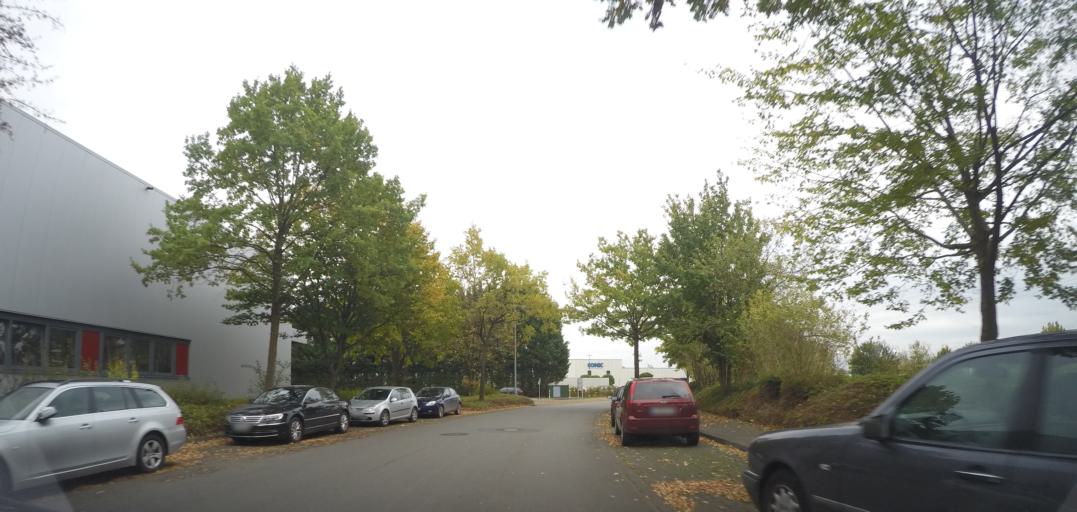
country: DE
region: North Rhine-Westphalia
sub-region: Regierungsbezirk Arnsberg
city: Lippstadt
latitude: 51.6757
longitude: 8.3762
